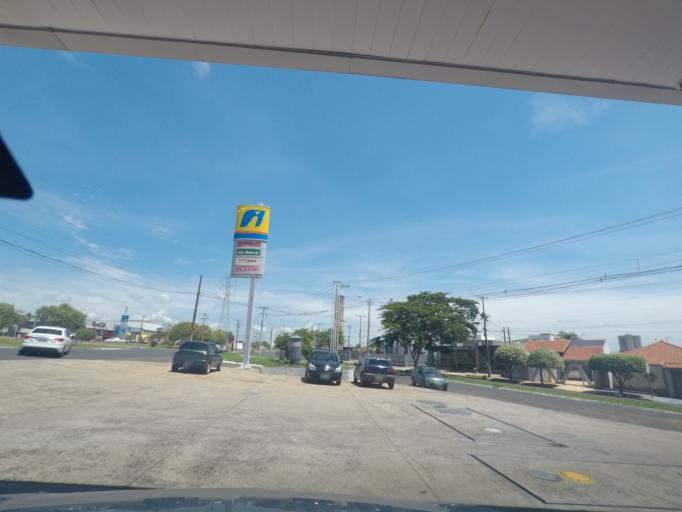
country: BR
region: Sao Paulo
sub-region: Matao
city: Matao
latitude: -21.6139
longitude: -48.3666
